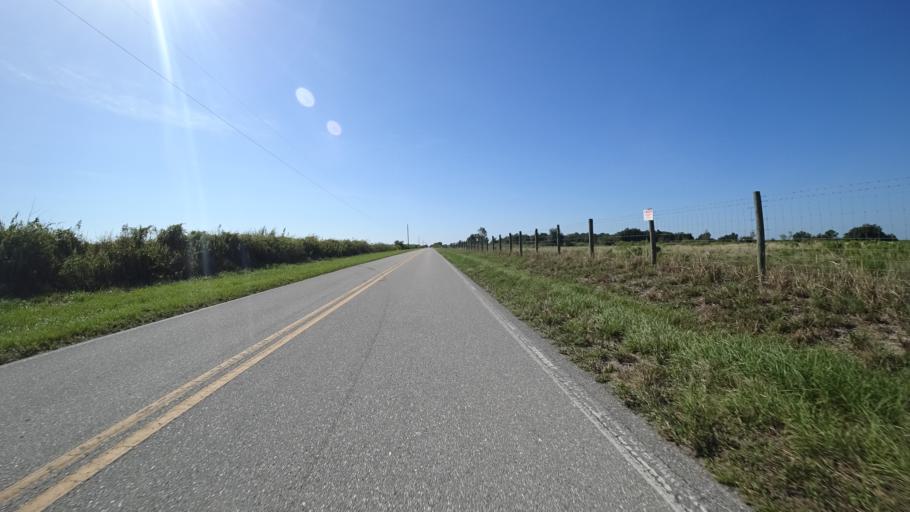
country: US
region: Florida
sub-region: Hillsborough County
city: Wimauma
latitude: 27.6154
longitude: -82.2927
